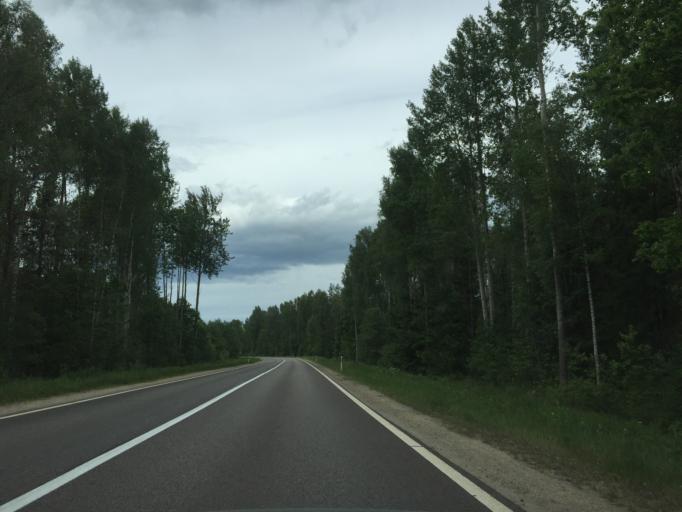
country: LV
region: Livani
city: Livani
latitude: 56.5326
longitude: 26.1402
